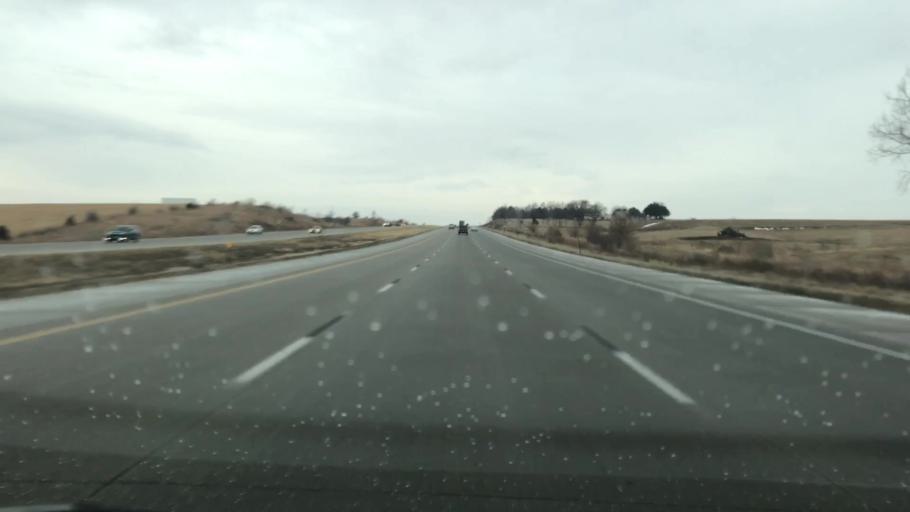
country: US
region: Nebraska
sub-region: Sarpy County
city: Gretna
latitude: 41.1324
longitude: -96.1817
